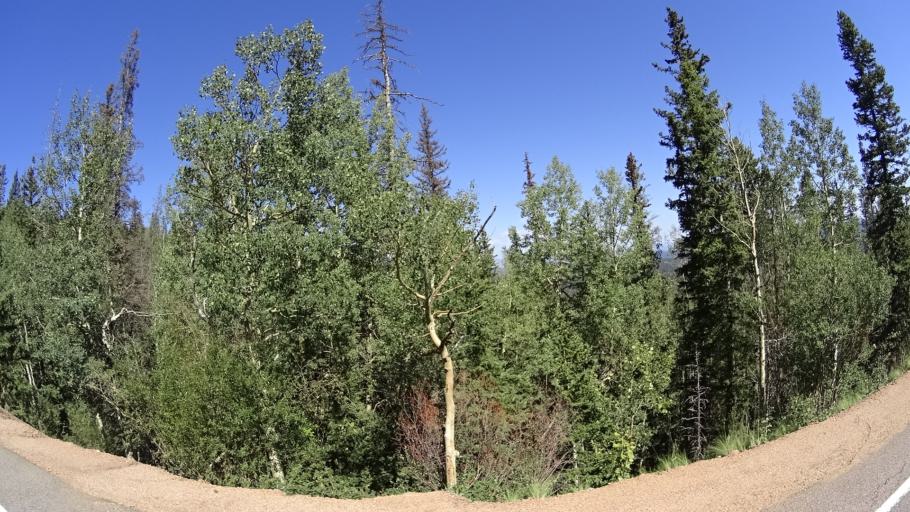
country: US
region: Colorado
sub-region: El Paso County
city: Cascade-Chipita Park
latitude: 38.8935
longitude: -105.0651
